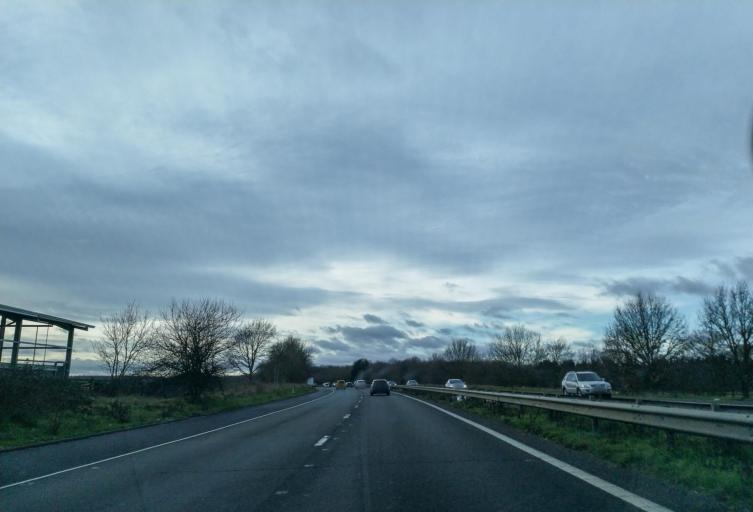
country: GB
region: England
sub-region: Kent
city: Faversham
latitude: 51.3027
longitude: 0.8481
